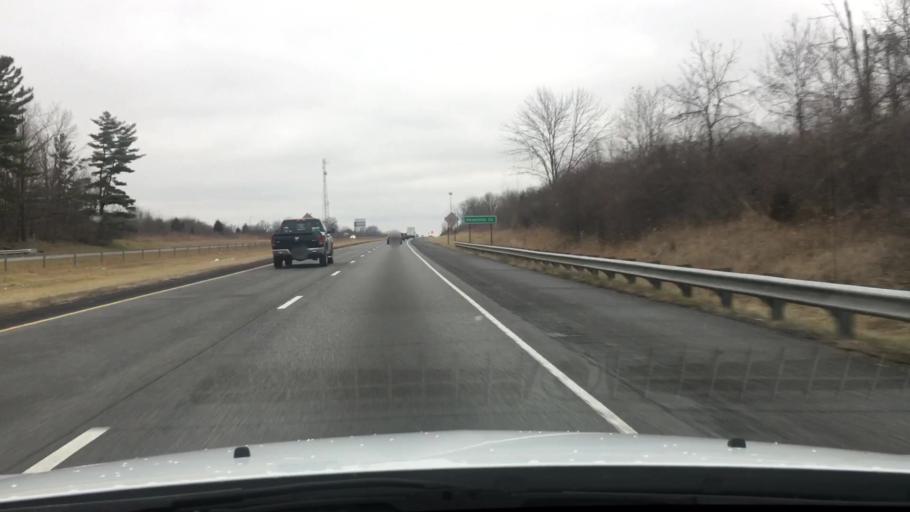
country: US
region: Indiana
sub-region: Boone County
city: Zionsville
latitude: 39.9150
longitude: -86.3255
